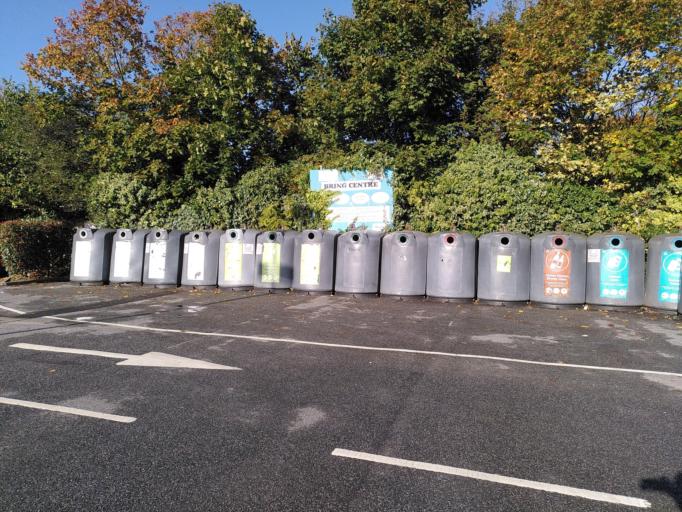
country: IE
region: Munster
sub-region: Waterford
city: Waterford
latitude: 52.2437
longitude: -7.0869
